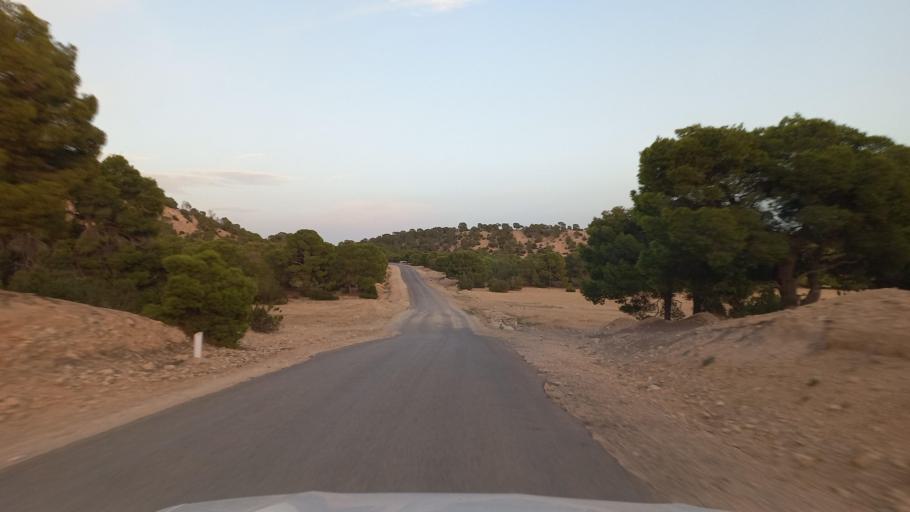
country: TN
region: Al Qasrayn
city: Sbiba
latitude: 35.4114
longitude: 8.9583
